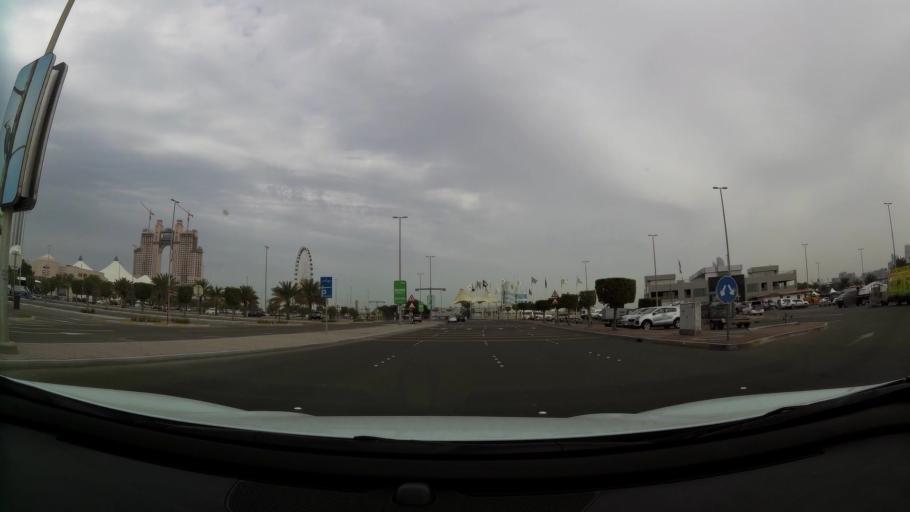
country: AE
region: Abu Dhabi
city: Abu Dhabi
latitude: 24.4727
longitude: 54.3229
